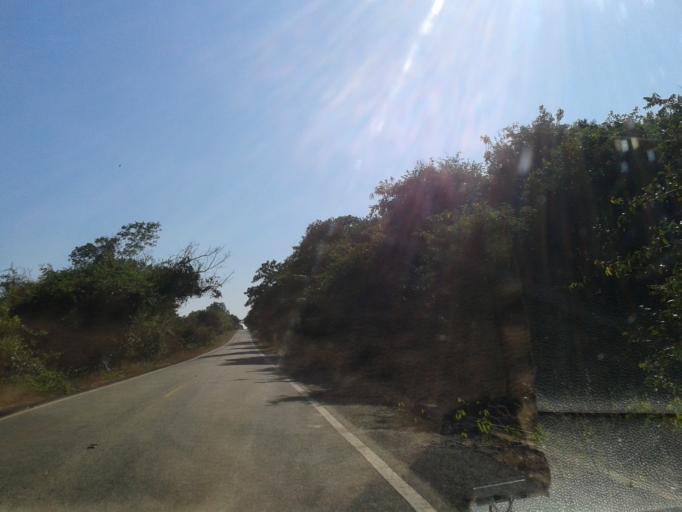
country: BR
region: Goias
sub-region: Mozarlandia
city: Mozarlandia
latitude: -14.6085
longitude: -50.5143
